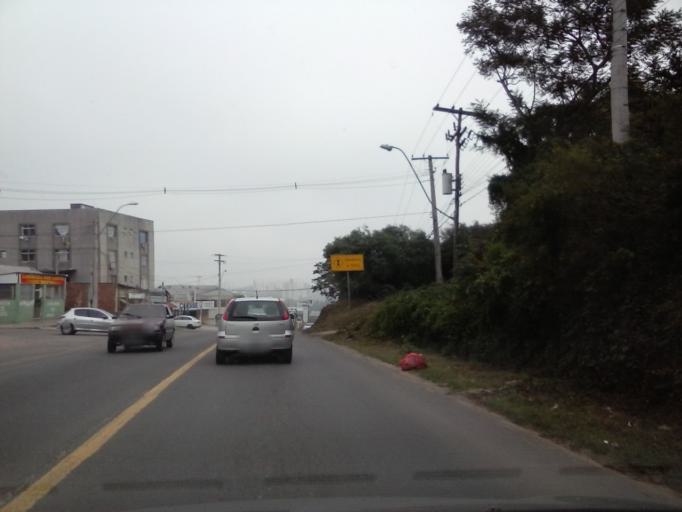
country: BR
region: Rio Grande do Sul
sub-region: Cachoeirinha
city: Cachoeirinha
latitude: -30.0385
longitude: -51.1205
